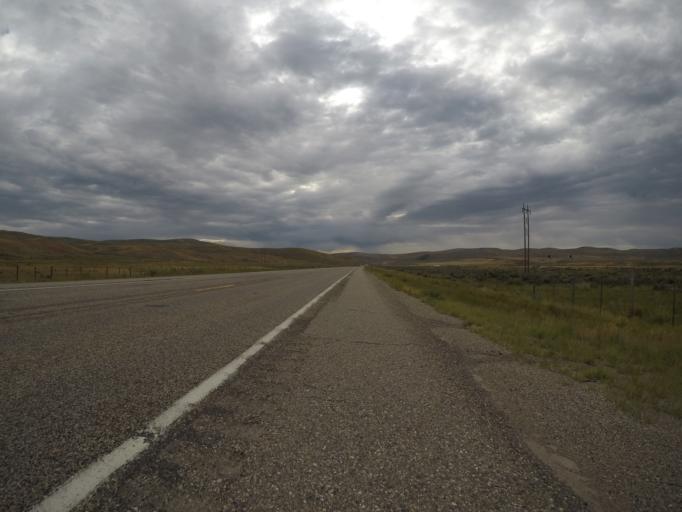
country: US
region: Utah
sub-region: Rich County
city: Randolph
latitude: 41.8239
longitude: -110.9031
